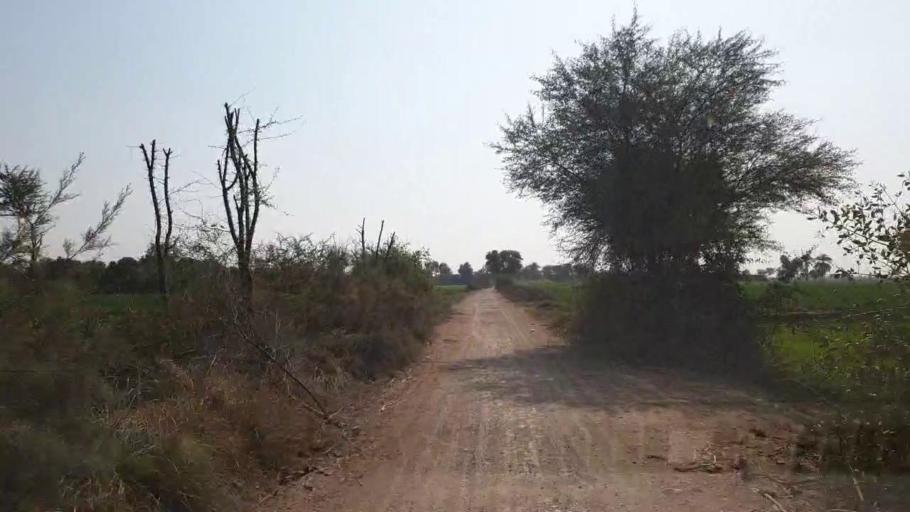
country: PK
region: Sindh
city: Shahdadpur
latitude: 25.9427
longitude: 68.4870
